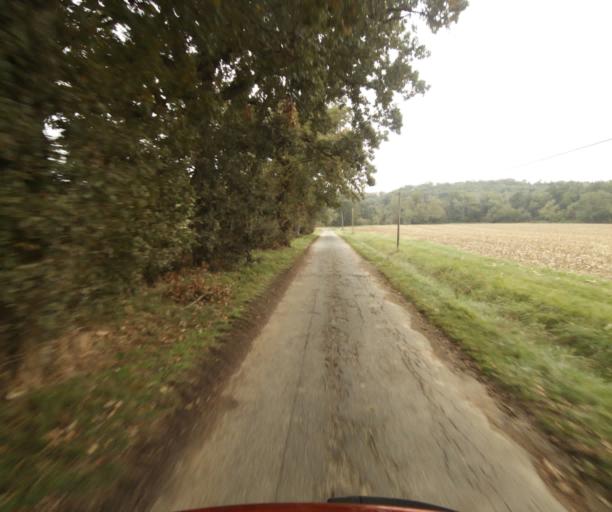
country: FR
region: Midi-Pyrenees
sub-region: Departement de la Haute-Garonne
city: Launac
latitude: 43.7779
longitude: 1.2261
